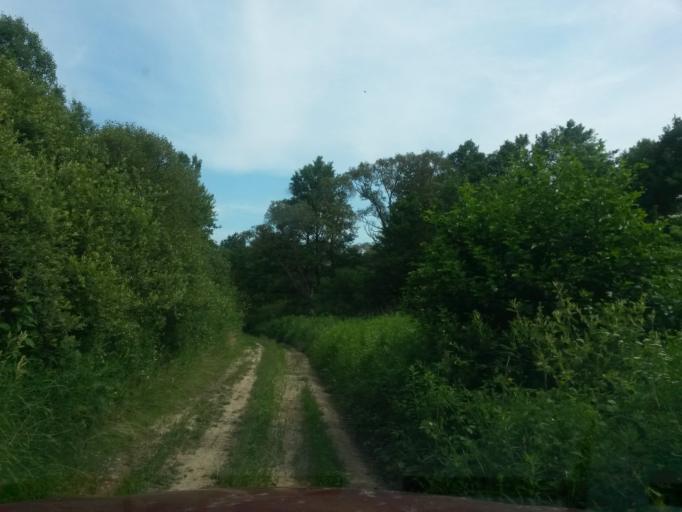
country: SK
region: Kosicky
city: Moldava nad Bodvou
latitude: 48.6511
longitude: 21.1064
